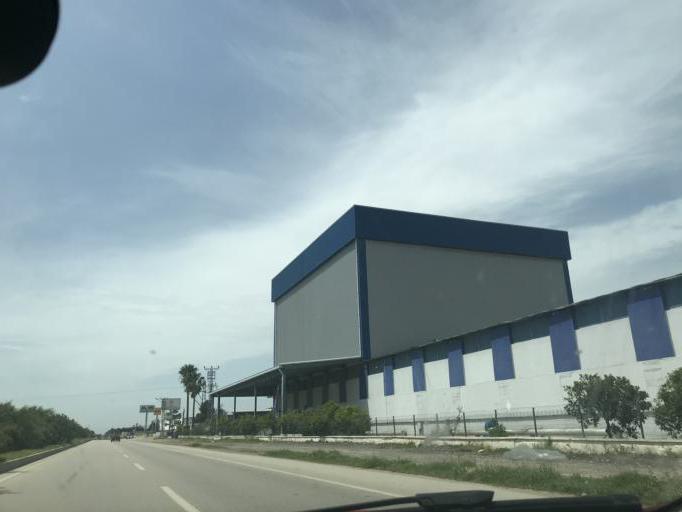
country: TR
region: Adana
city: Yakapinar
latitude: 36.9701
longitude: 35.5315
